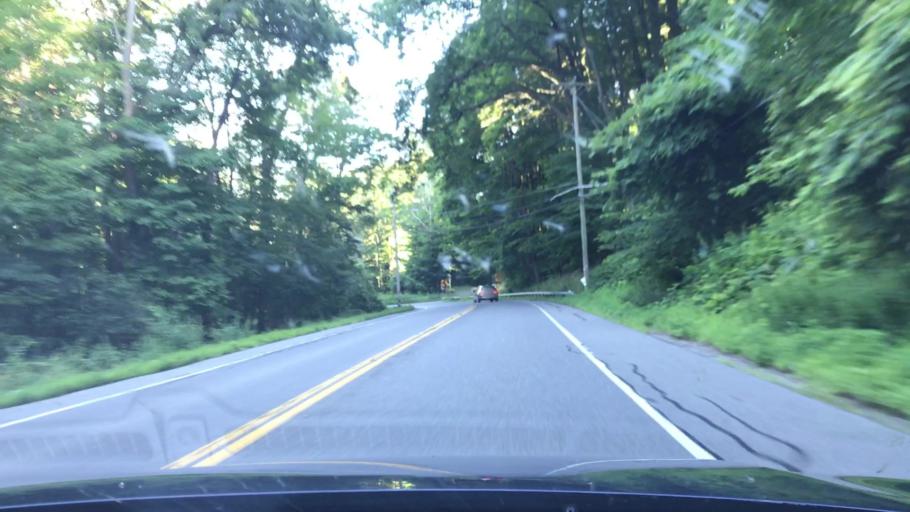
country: US
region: New York
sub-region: Westchester County
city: Heritage Hills
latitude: 41.3697
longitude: -73.6961
